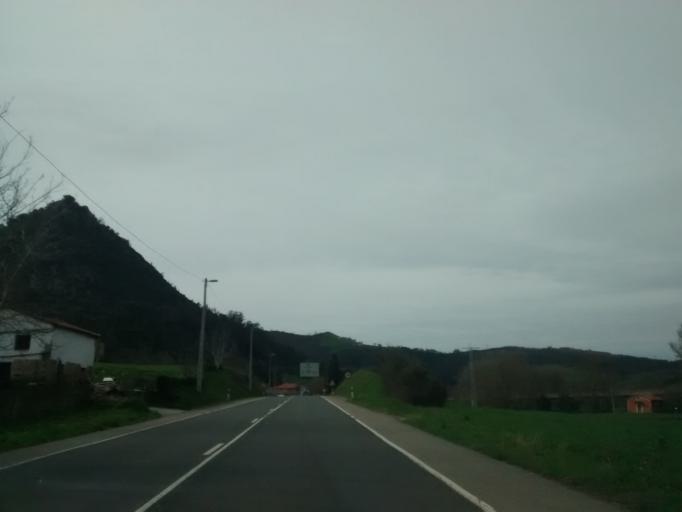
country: ES
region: Cantabria
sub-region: Provincia de Cantabria
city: Puente Viesgo
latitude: 43.2871
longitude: -3.9562
